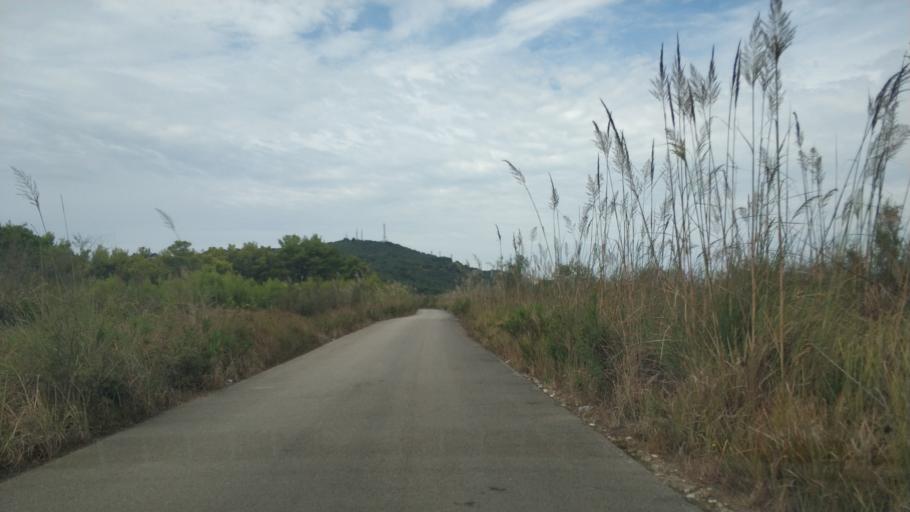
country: AL
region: Vlore
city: Vlore
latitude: 40.5034
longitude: 19.4261
